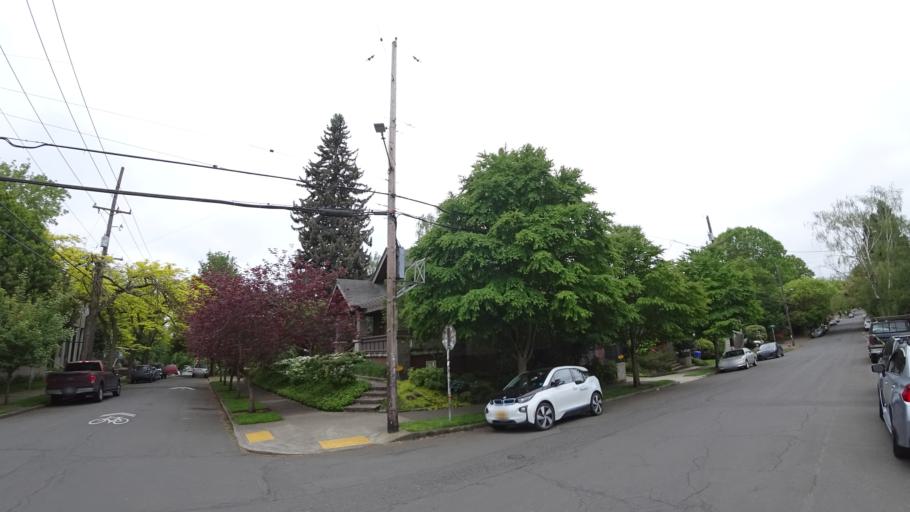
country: US
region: Oregon
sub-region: Multnomah County
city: Portland
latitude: 45.5207
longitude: -122.6350
